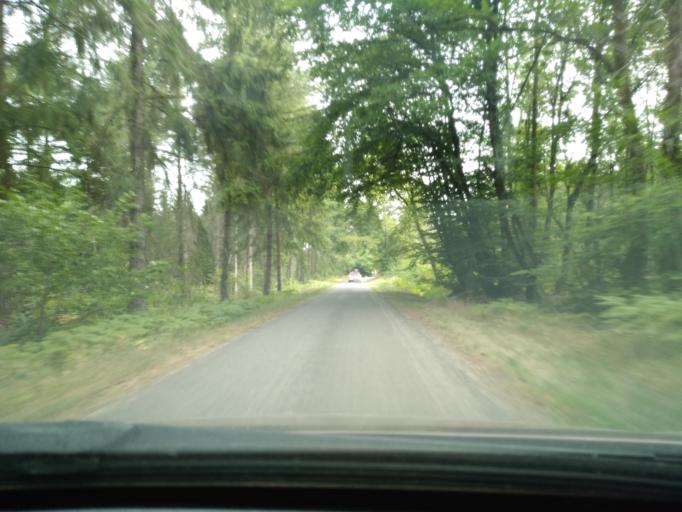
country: FR
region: Bourgogne
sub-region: Departement de la Cote-d'Or
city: Saulieu
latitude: 47.3463
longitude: 4.0919
